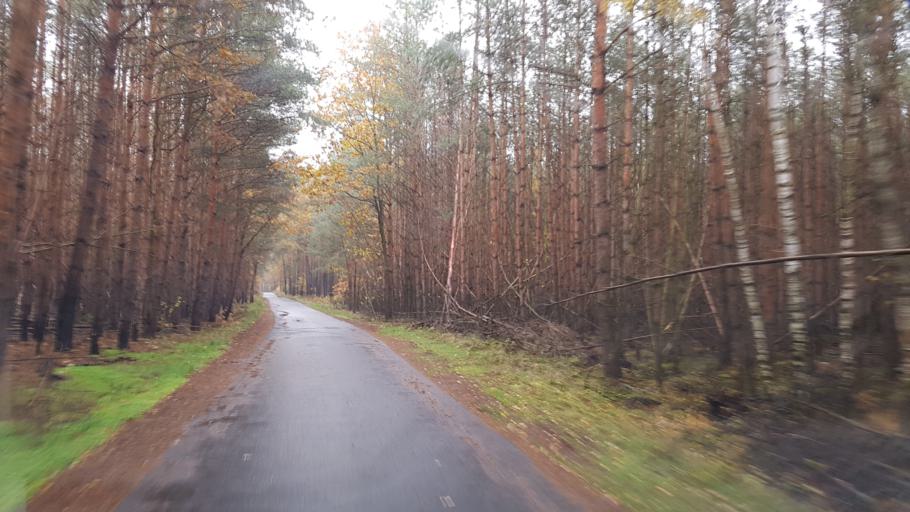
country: DE
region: Brandenburg
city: Herzberg
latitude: 51.6558
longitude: 13.2479
